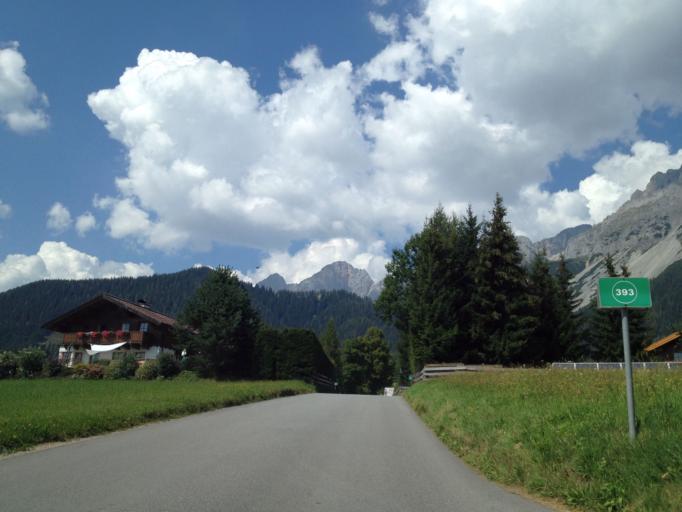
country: AT
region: Styria
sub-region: Politischer Bezirk Liezen
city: Schladming
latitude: 47.4235
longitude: 13.6353
